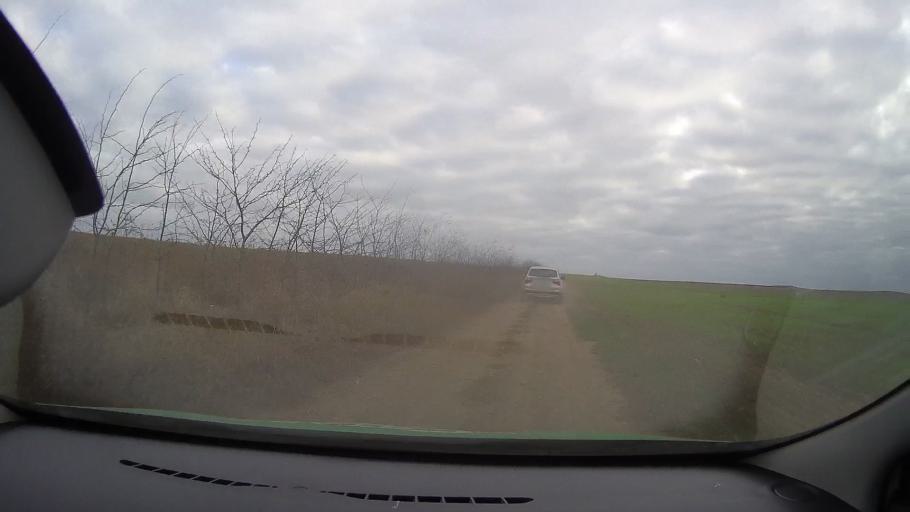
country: RO
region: Tulcea
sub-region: Comuna Jurilovca
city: Jurilovca
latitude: 44.7700
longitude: 28.9068
